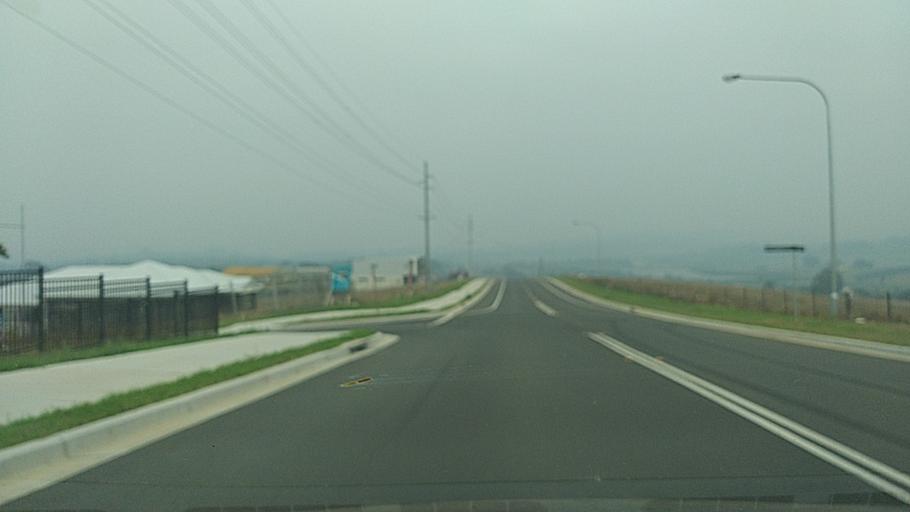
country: AU
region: New South Wales
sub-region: Shellharbour
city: Croom
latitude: -34.5975
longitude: 150.8473
